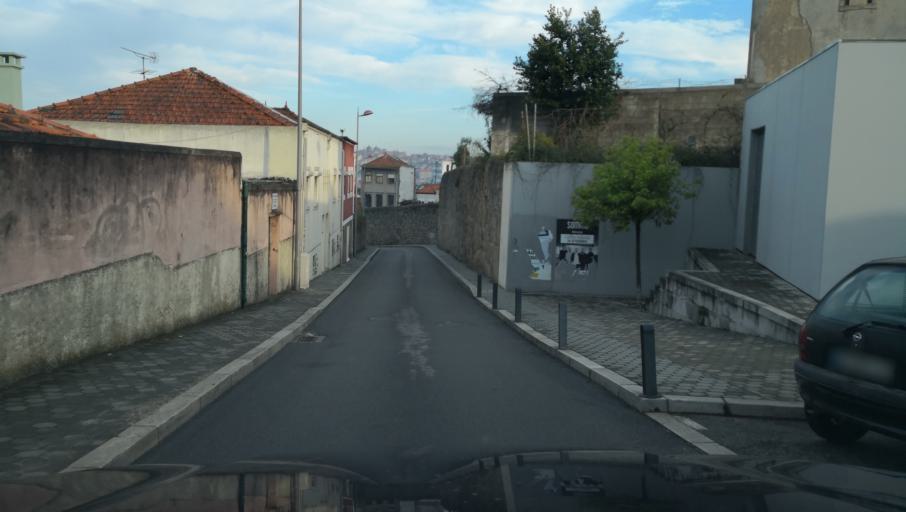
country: PT
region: Porto
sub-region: Vila Nova de Gaia
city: Vila Nova de Gaia
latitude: 41.1336
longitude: -8.6085
